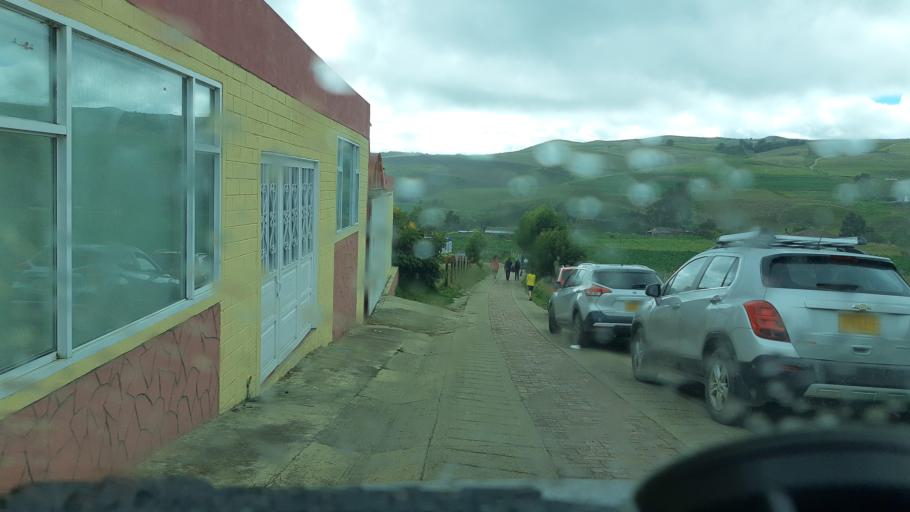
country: CO
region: Boyaca
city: Cucaita
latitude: 5.5045
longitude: -73.4318
